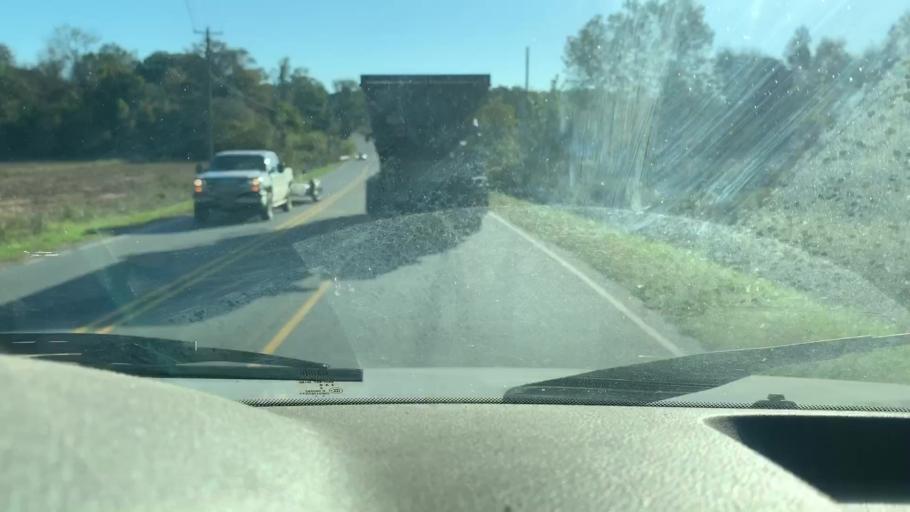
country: US
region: North Carolina
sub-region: Mecklenburg County
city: Huntersville
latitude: 35.4084
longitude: -80.7328
